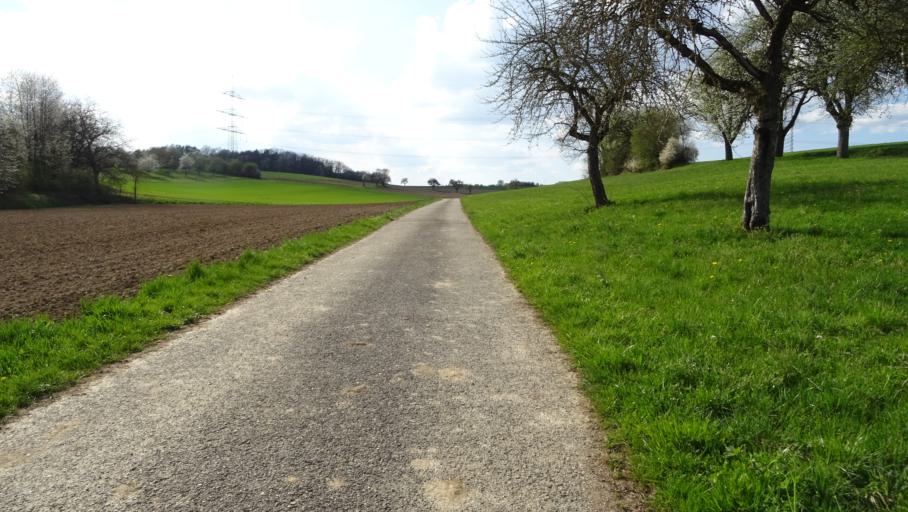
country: DE
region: Baden-Wuerttemberg
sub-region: Karlsruhe Region
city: Billigheim
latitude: 49.3981
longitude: 9.2559
